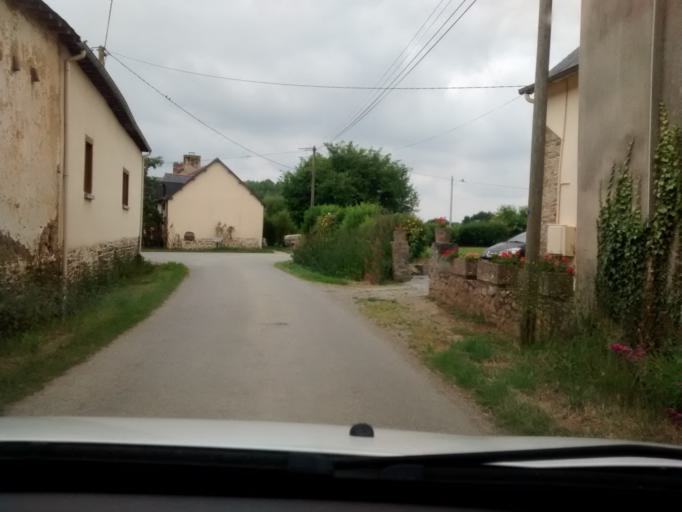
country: FR
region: Brittany
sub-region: Departement d'Ille-et-Vilaine
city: Servon-sur-Vilaine
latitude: 48.1420
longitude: -1.4812
